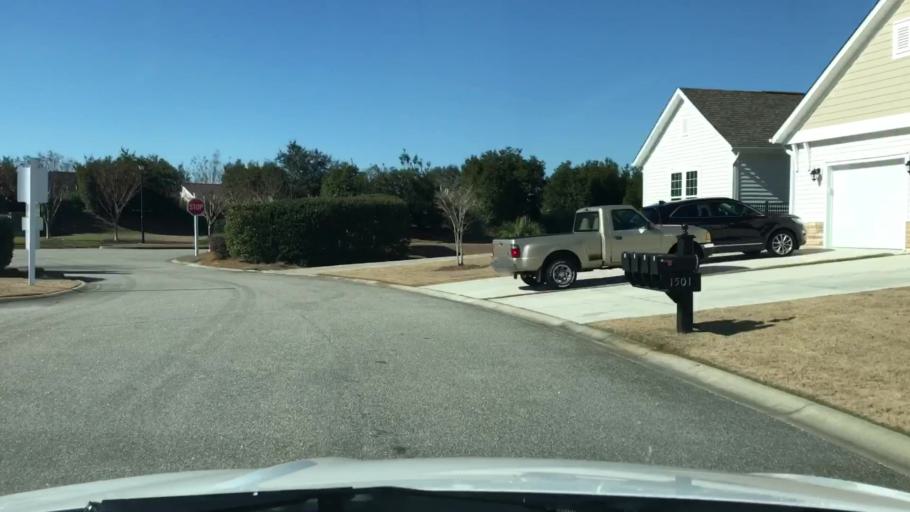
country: US
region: South Carolina
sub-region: Horry County
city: Socastee
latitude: 33.6463
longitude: -79.0369
